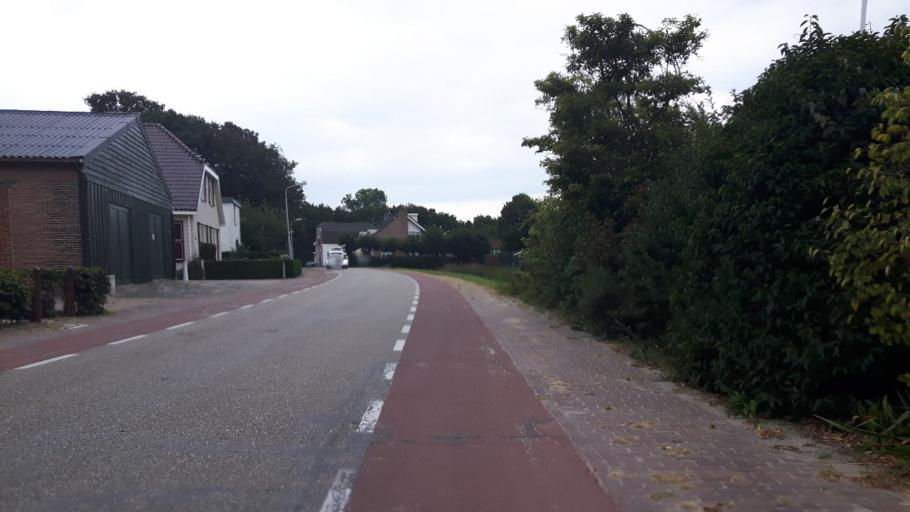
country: NL
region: South Holland
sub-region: Gemeente Hillegom
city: Hillegom
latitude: 52.3090
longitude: 4.5553
